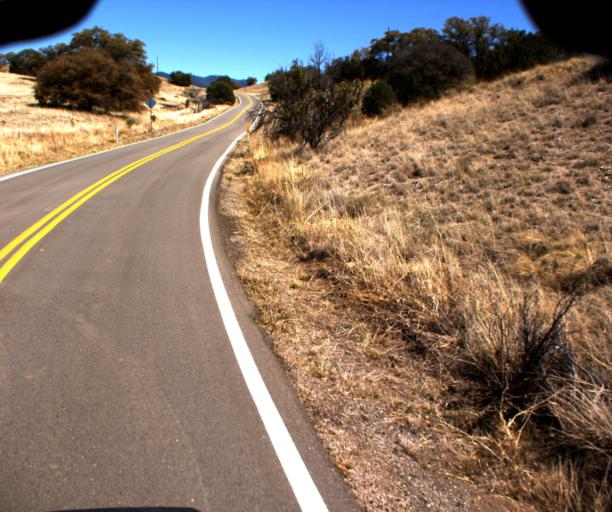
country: US
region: Arizona
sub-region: Cochise County
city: Huachuca City
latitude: 31.5442
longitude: -110.5244
